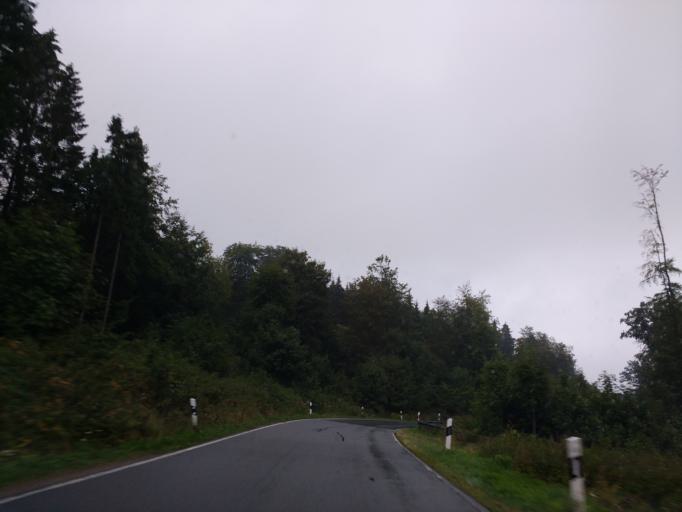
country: DE
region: Lower Saxony
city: Heyen
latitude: 52.0514
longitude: 9.5050
